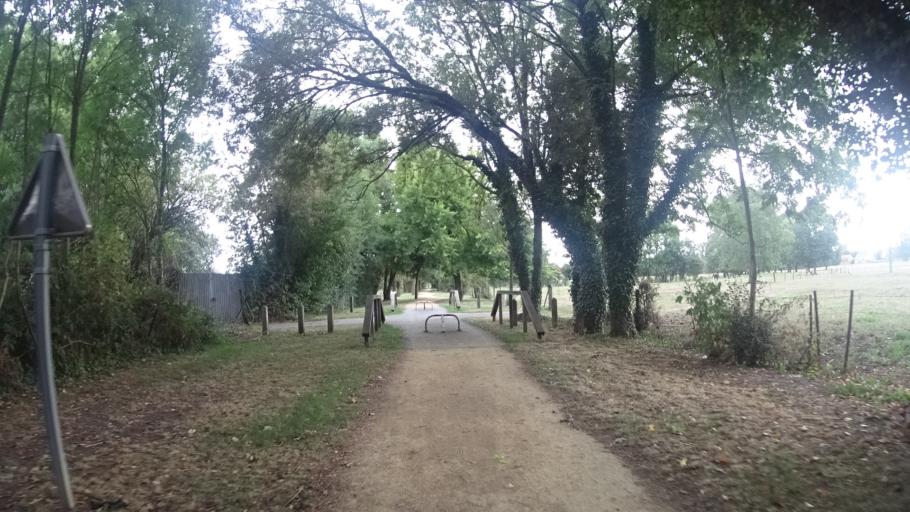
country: FR
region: Picardie
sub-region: Departement de l'Aisne
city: Origny-Sainte-Benoite
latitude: 49.8425
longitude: 3.4883
